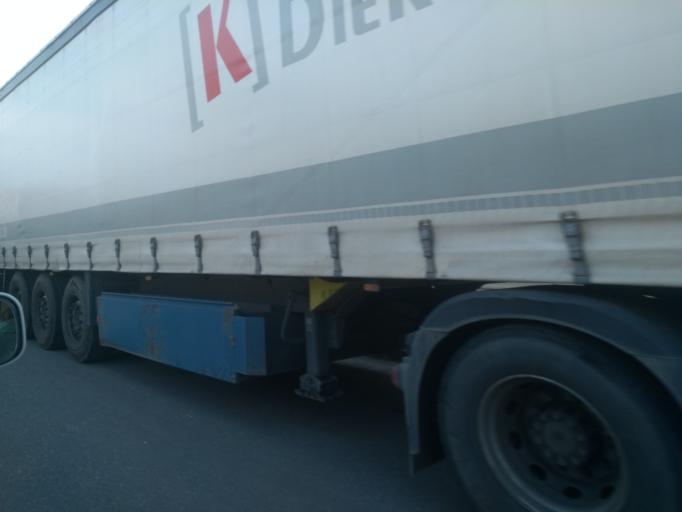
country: GE
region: Ajaria
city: Batumi
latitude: 41.6373
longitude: 41.6211
